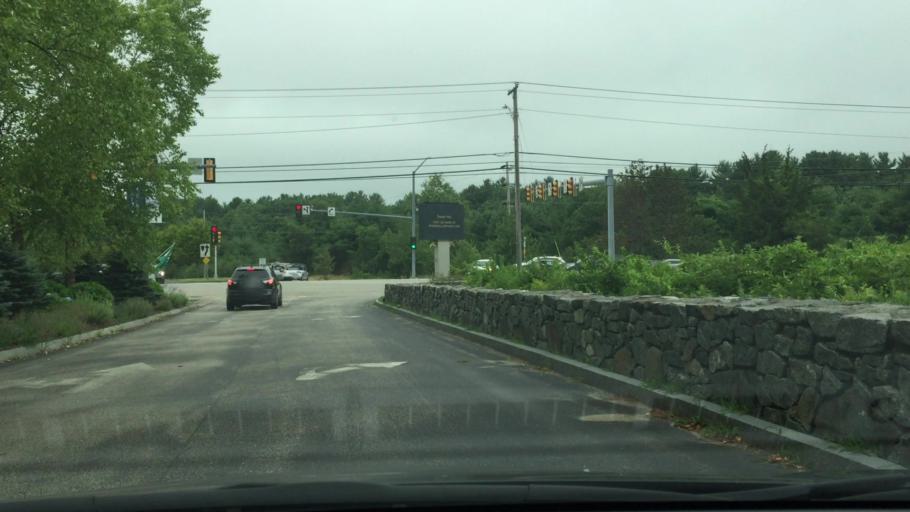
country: US
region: Maine
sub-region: York County
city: York Harbor
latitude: 43.1542
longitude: -70.6582
